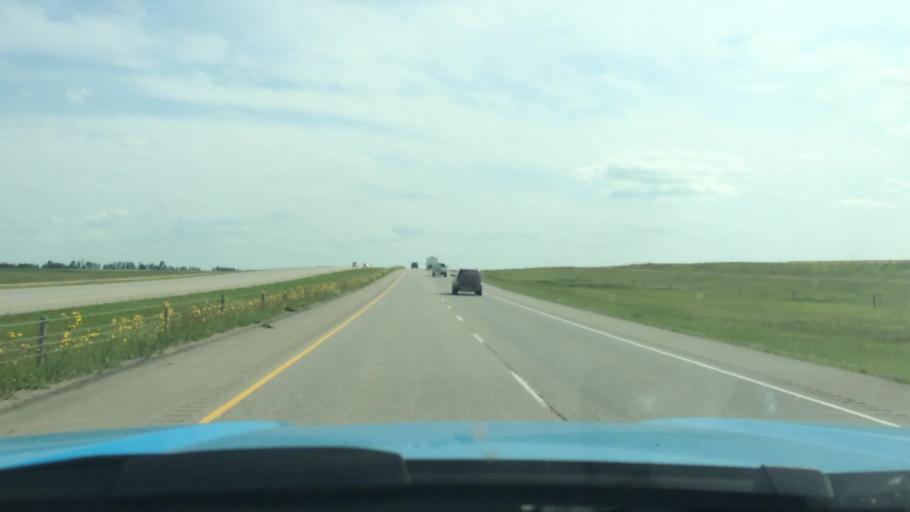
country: CA
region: Alberta
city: Carstairs
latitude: 51.6334
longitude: -114.0256
